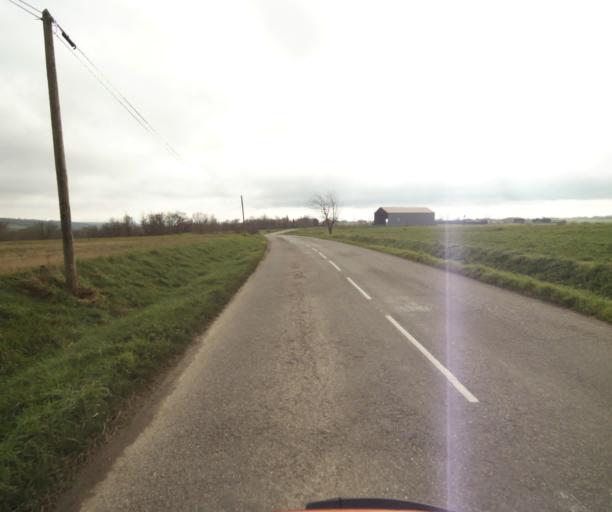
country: FR
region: Languedoc-Roussillon
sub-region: Departement de l'Aude
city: Belpech
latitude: 43.1979
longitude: 1.7324
